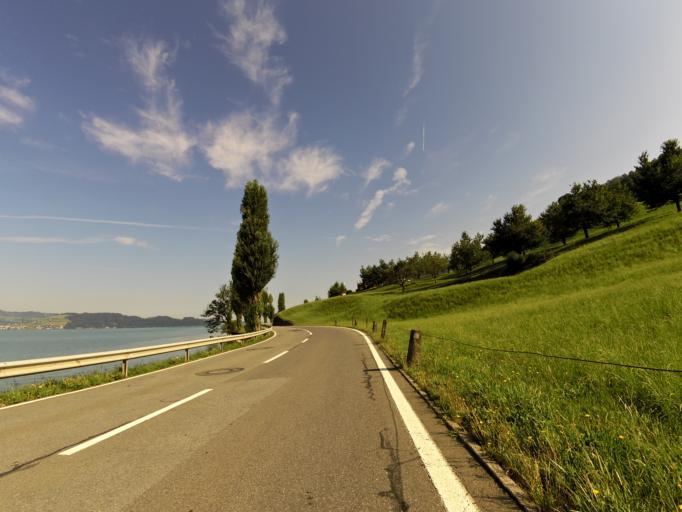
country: CH
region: Schwyz
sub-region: Bezirk Schwyz
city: Arth
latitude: 47.0791
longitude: 8.5249
